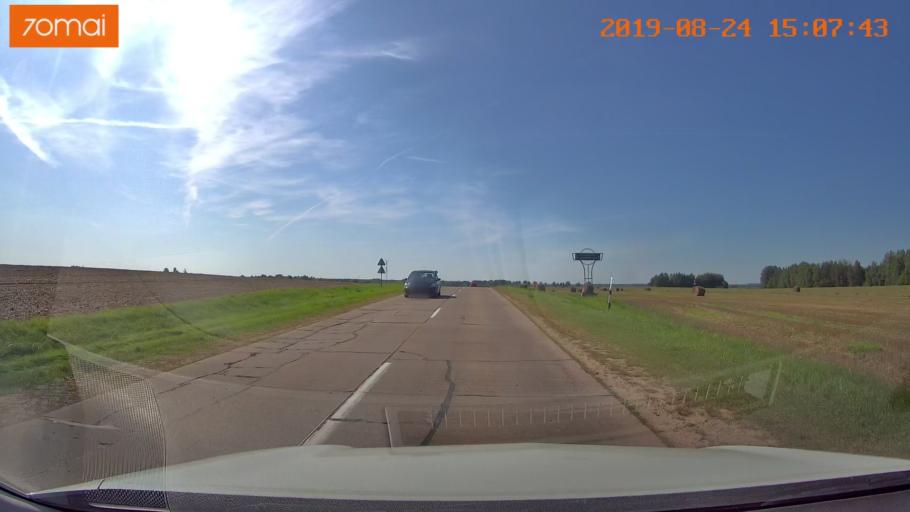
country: BY
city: Michanovichi
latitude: 53.6083
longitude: 27.6709
